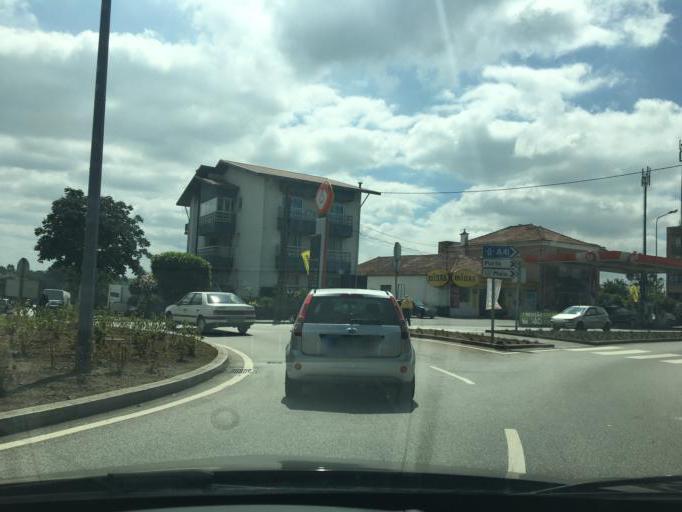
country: PT
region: Porto
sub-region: Maia
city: Anta
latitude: 41.2601
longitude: -8.6164
